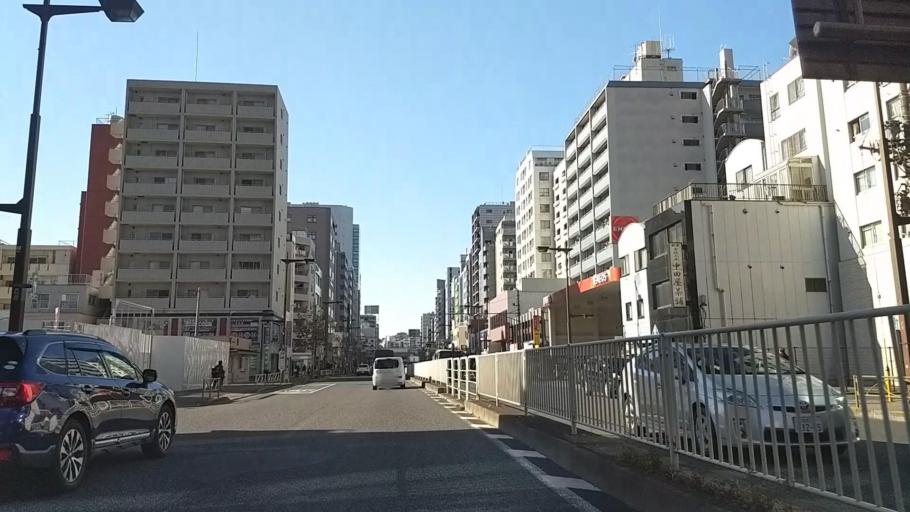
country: JP
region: Tokyo
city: Urayasu
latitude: 35.6945
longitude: 139.7964
